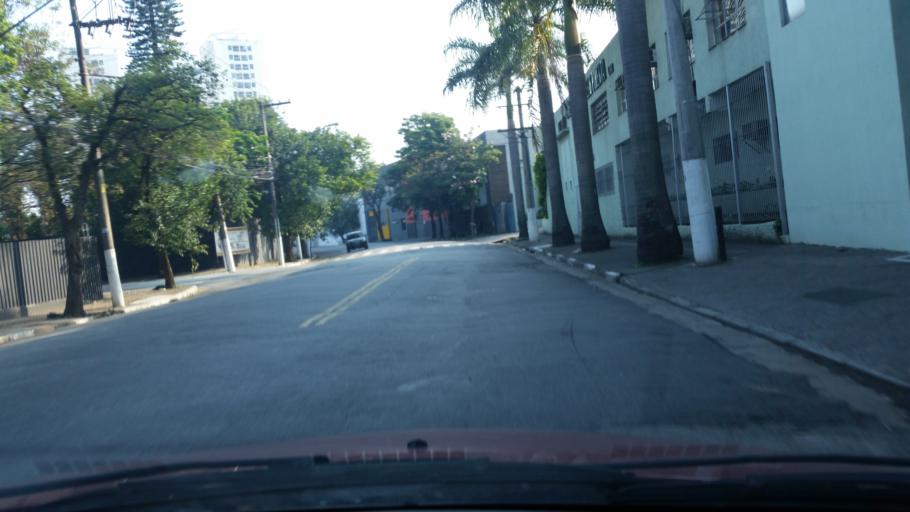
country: BR
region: Sao Paulo
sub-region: Osasco
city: Osasco
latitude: -23.5298
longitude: -46.7437
